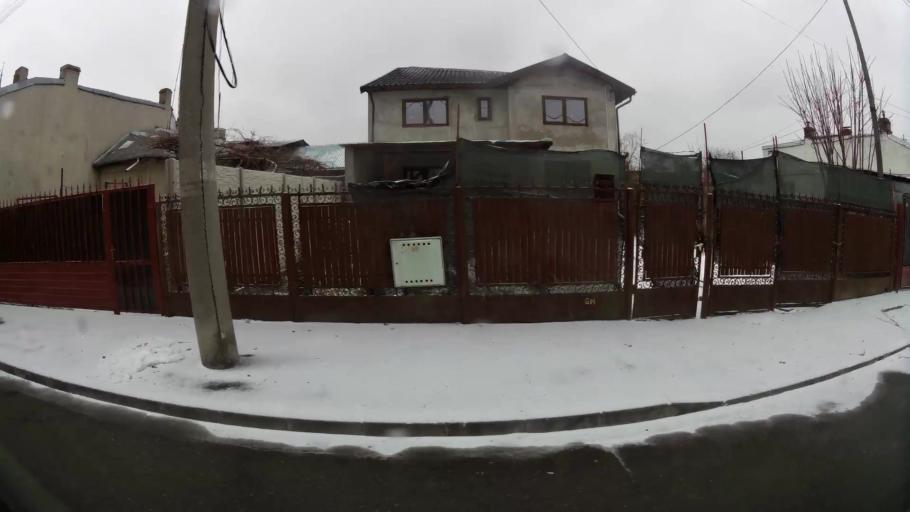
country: RO
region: Prahova
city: Ploiesti
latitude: 44.9498
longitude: 26.0158
